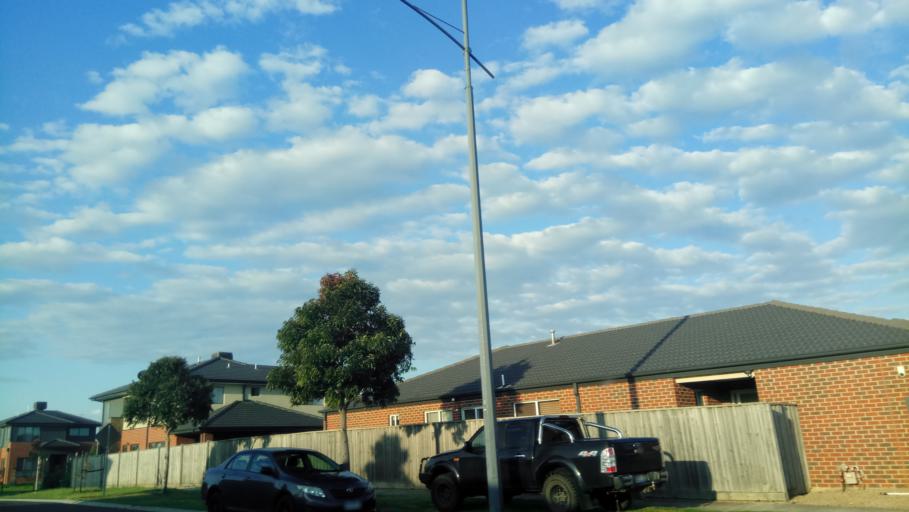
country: AU
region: Victoria
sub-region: Wyndham
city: Point Cook
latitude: -37.9053
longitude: 144.7592
